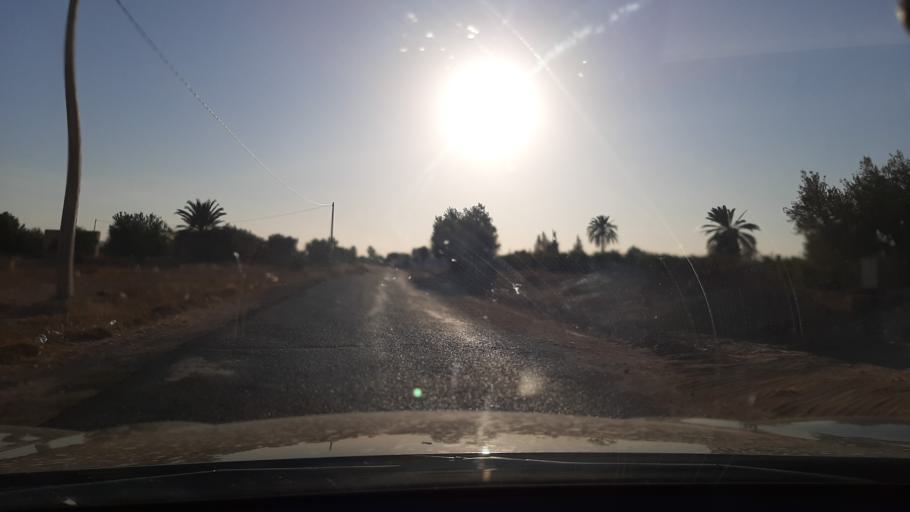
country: TN
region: Qabis
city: Matmata
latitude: 33.6175
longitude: 10.2619
